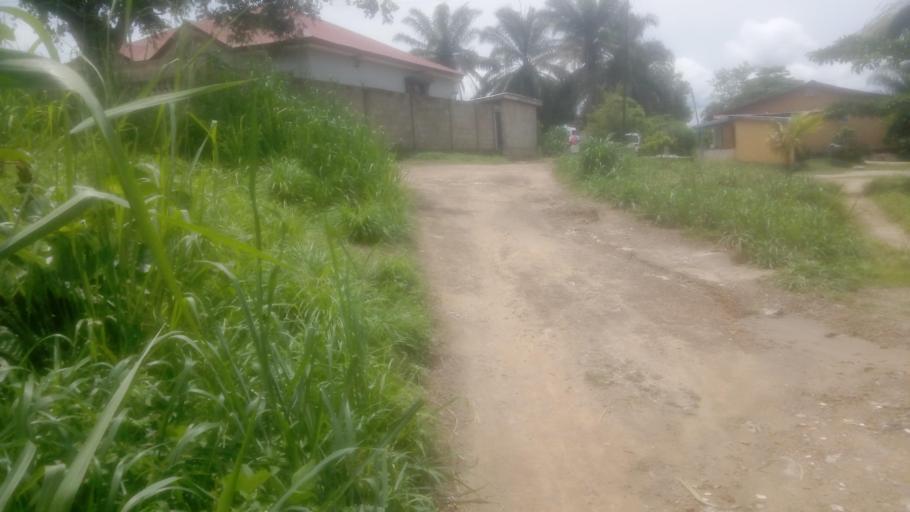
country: SL
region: Southern Province
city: Bo
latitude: 7.9520
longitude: -11.7118
